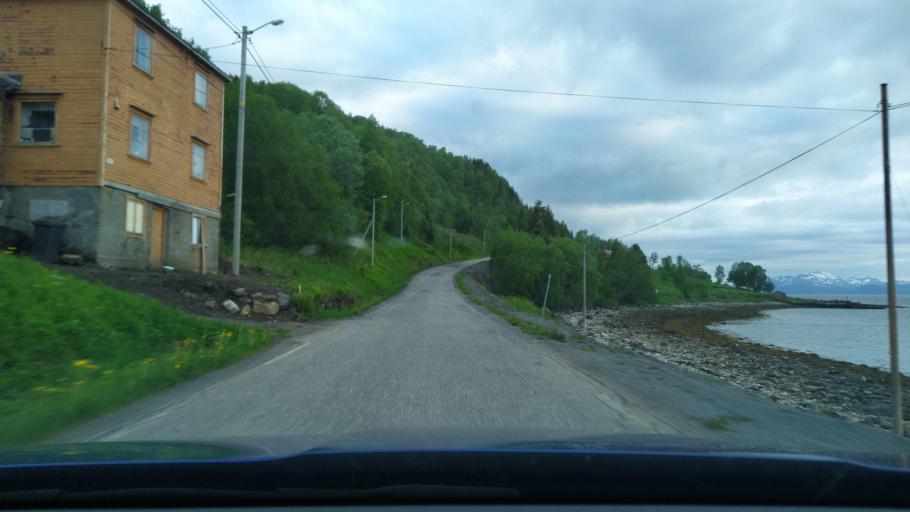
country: NO
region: Troms
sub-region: Lenvik
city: Finnsnes
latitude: 69.1342
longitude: 17.8949
